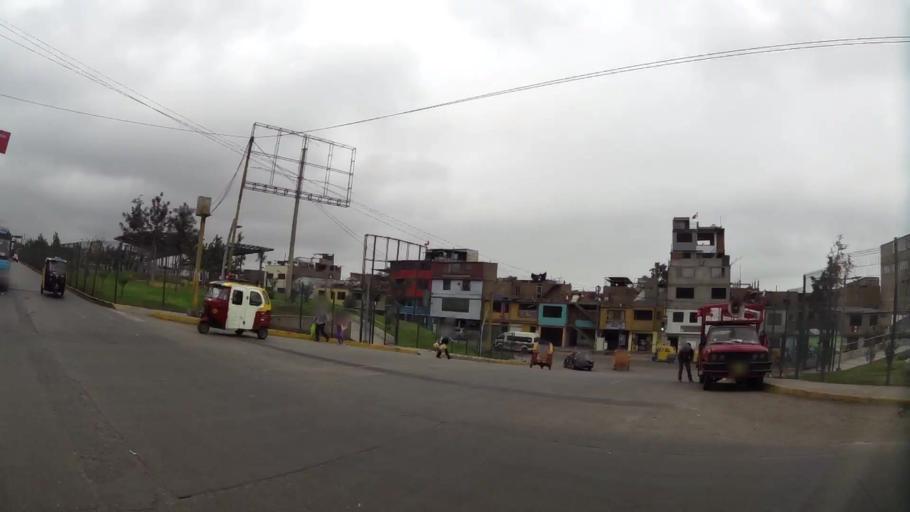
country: PE
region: Lima
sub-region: Lima
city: Surco
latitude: -12.1443
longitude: -76.9728
